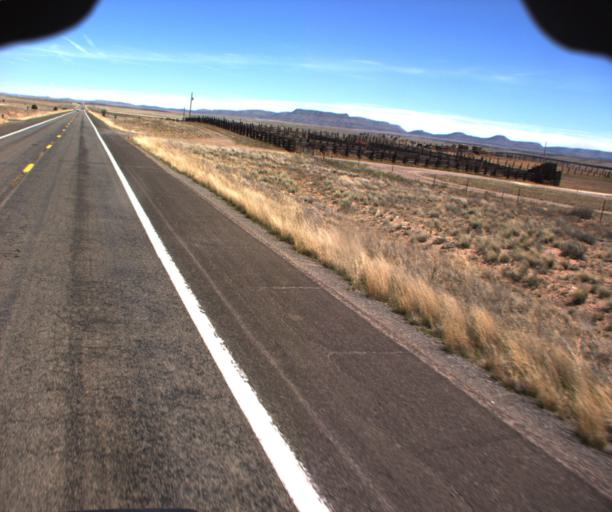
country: US
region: Arizona
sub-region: Mohave County
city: Peach Springs
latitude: 35.4637
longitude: -113.6070
